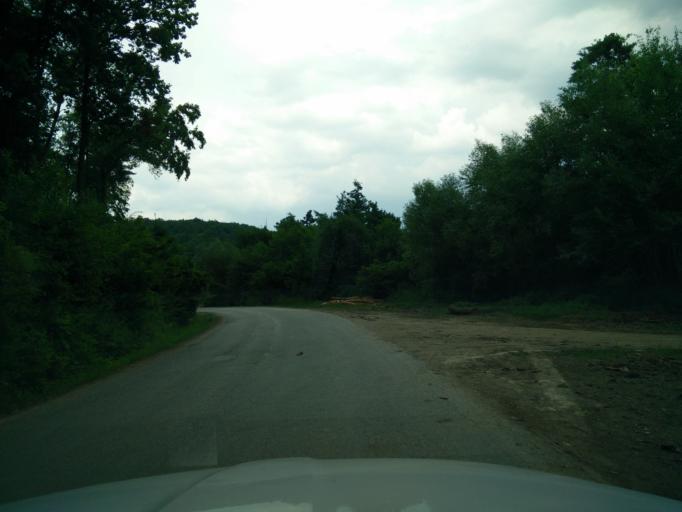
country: SK
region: Nitriansky
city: Novaky
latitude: 48.7367
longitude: 18.5471
